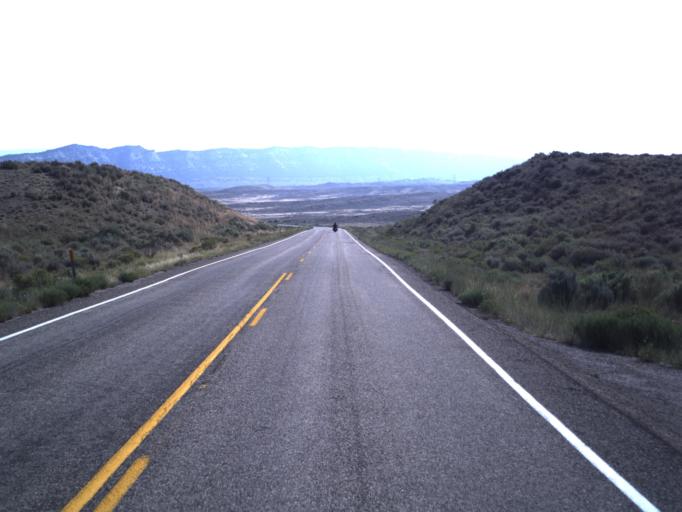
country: US
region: Utah
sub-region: Daggett County
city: Manila
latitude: 40.9776
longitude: -109.4556
